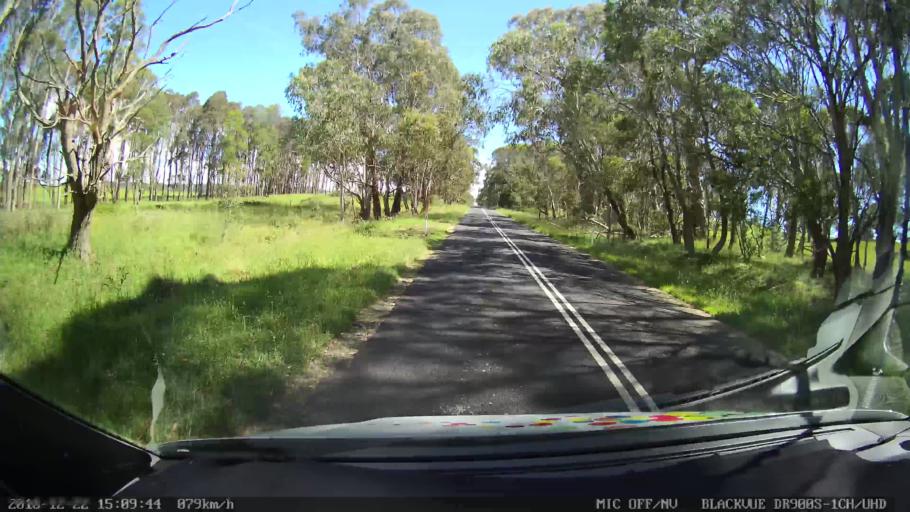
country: AU
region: New South Wales
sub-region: Bellingen
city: Dorrigo
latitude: -30.3268
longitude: 152.4065
